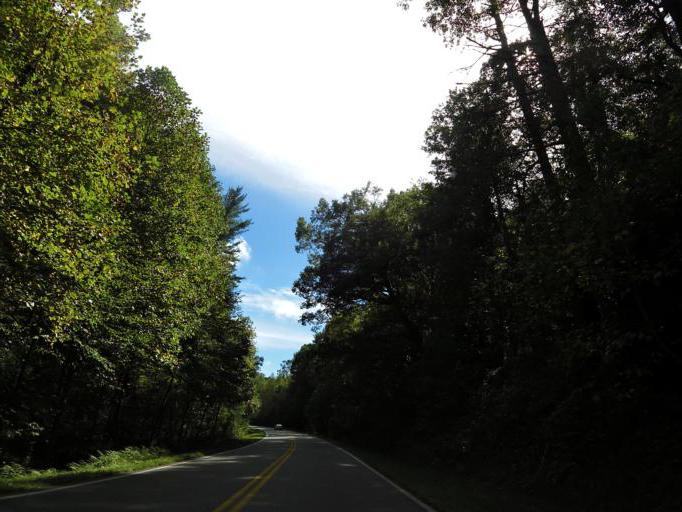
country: US
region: Georgia
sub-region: Pickens County
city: Nelson
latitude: 34.4416
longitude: -84.2791
